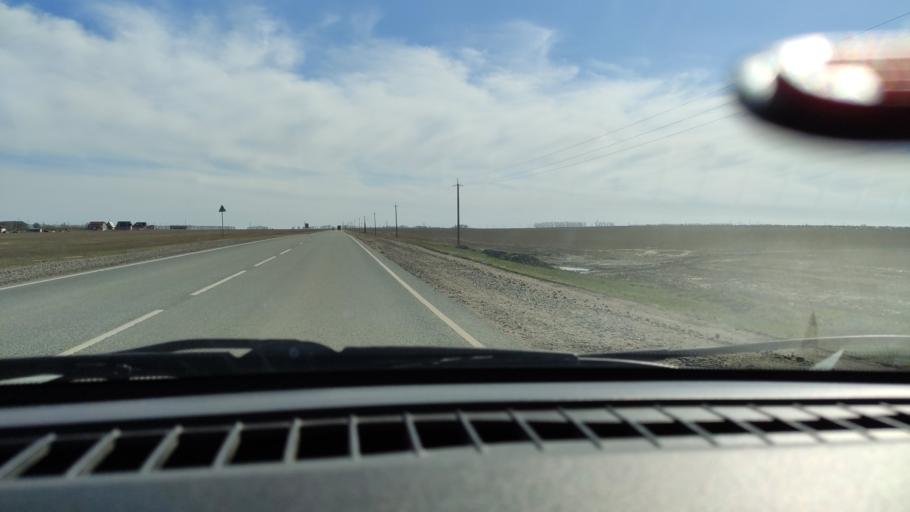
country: RU
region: Bashkortostan
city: Sterlitamak
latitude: 53.6348
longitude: 55.8393
